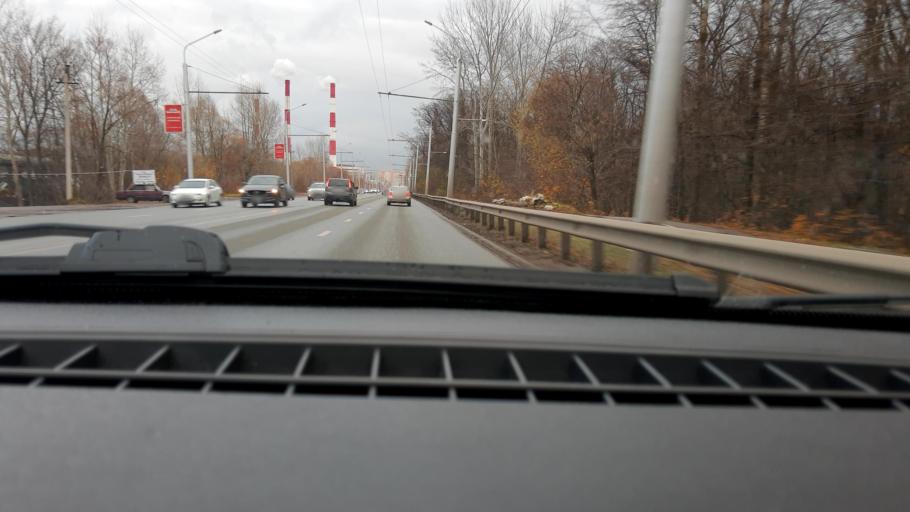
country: RU
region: Bashkortostan
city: Ufa
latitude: 54.7887
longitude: 56.0973
